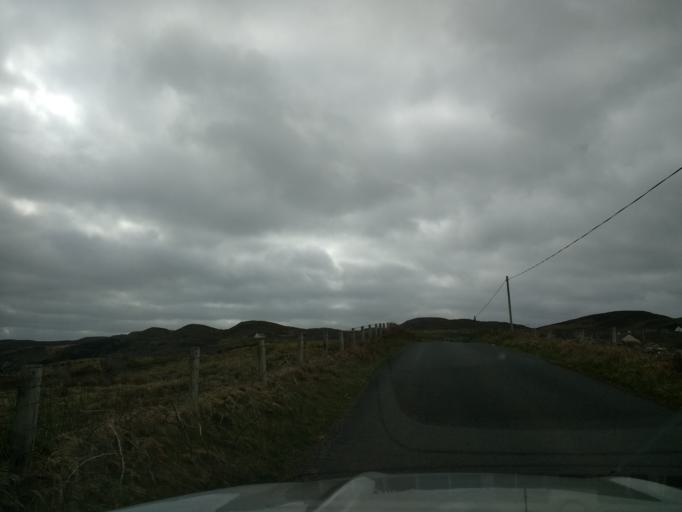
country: IE
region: Ulster
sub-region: County Donegal
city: Buncrana
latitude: 55.2750
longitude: -7.6386
